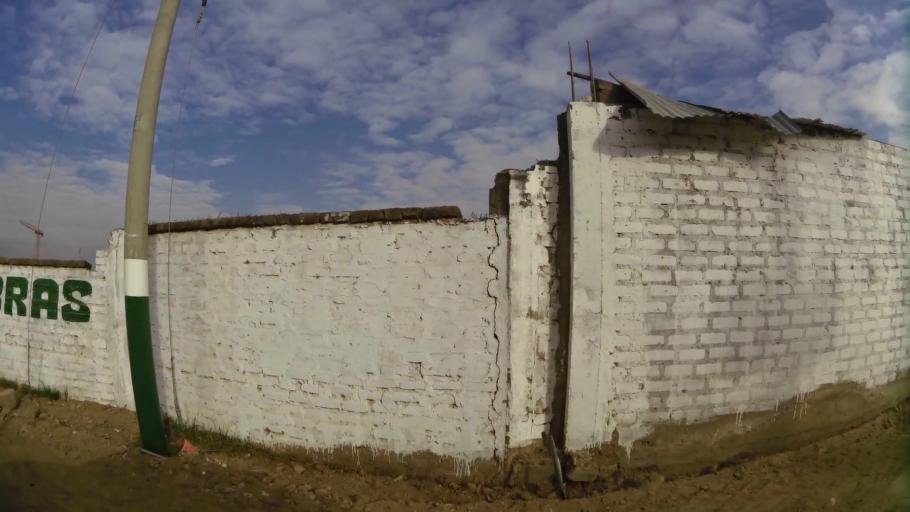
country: PE
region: Junin
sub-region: Provincia de Huancayo
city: Huancayo
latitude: -12.0435
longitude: -75.1921
